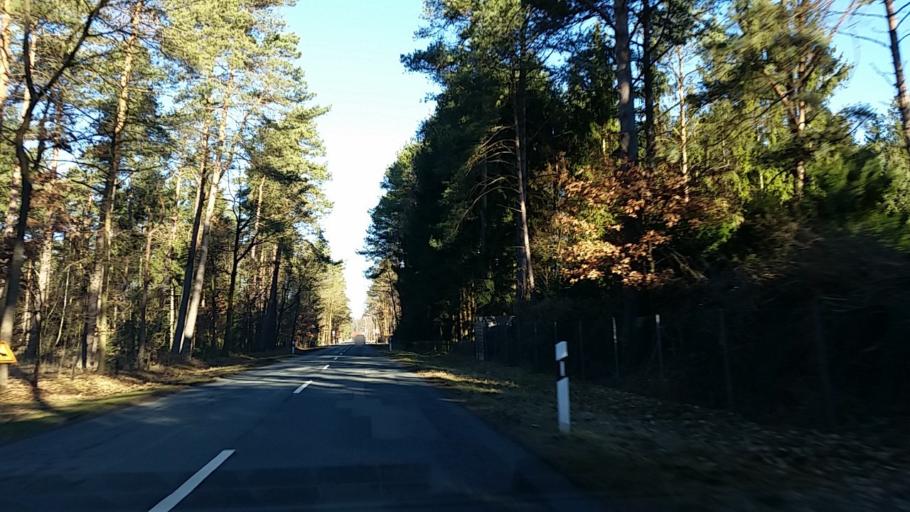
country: DE
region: Lower Saxony
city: Sassenburg
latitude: 52.5466
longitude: 10.6805
